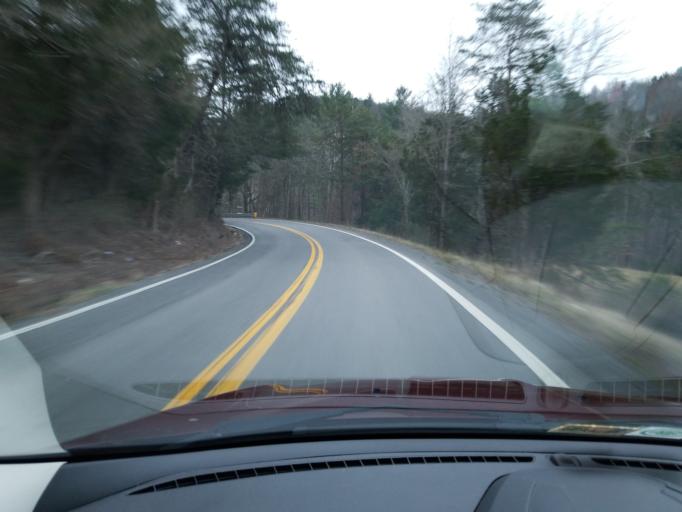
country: US
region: West Virginia
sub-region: Monroe County
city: Union
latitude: 37.4997
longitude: -80.6112
